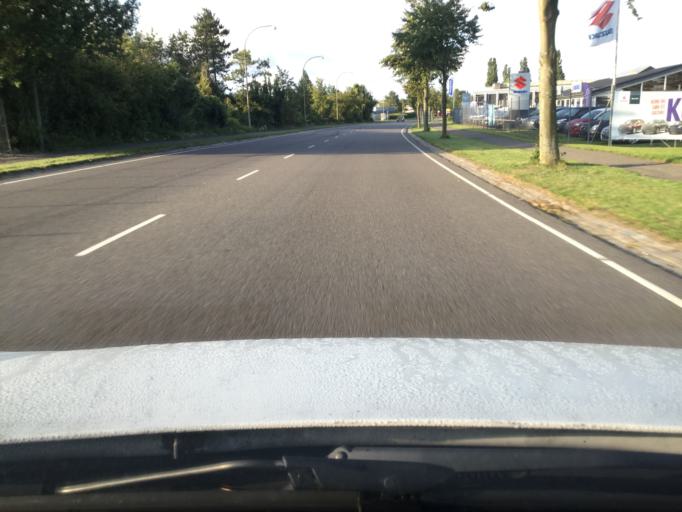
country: DK
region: Zealand
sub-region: Lolland Kommune
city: Nakskov
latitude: 54.8286
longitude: 11.1624
